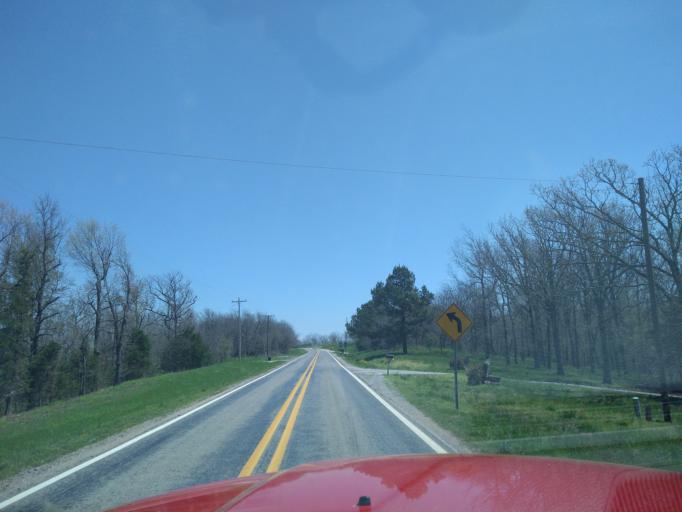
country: US
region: Arkansas
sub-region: Washington County
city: West Fork
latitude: 35.8721
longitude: -94.2473
